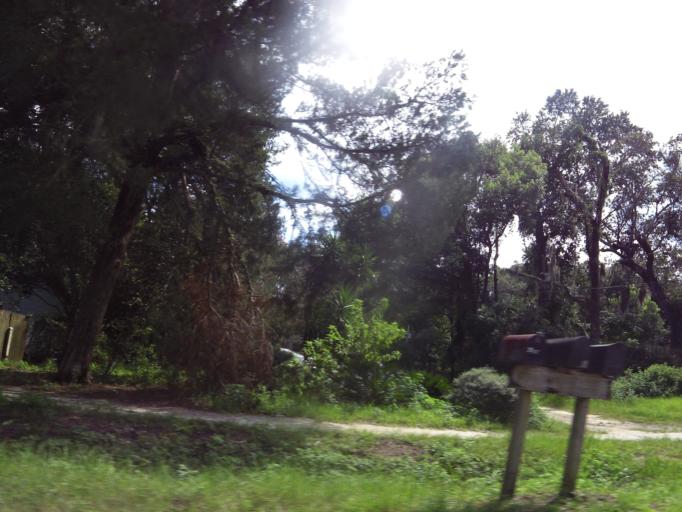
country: US
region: Florida
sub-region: Clay County
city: Lakeside
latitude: 30.1237
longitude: -81.7651
